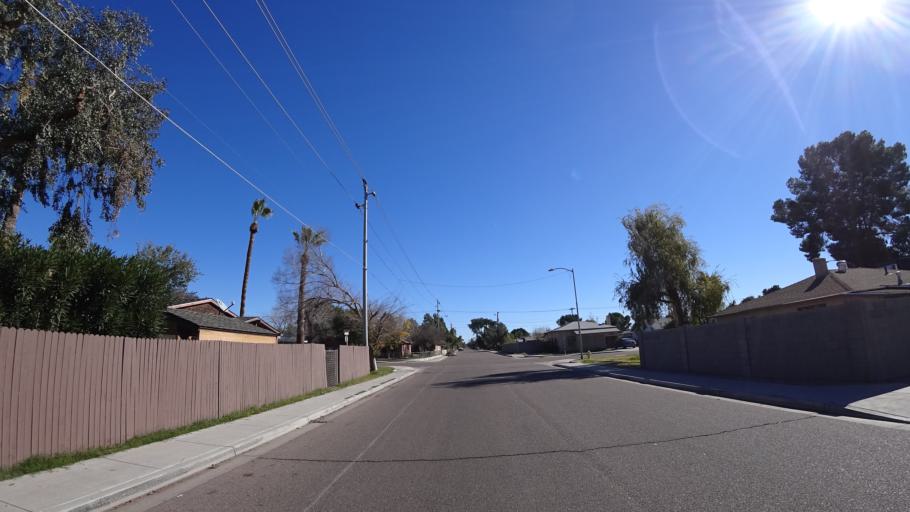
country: US
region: Arizona
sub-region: Maricopa County
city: Phoenix
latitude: 33.5038
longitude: -112.0611
